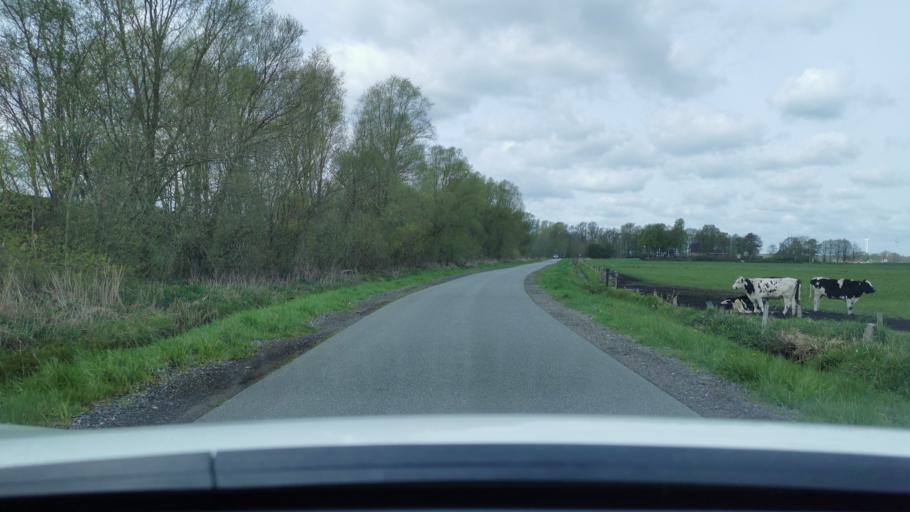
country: DE
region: Schleswig-Holstein
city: Oldenbuttel
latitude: 54.1819
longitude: 9.4477
